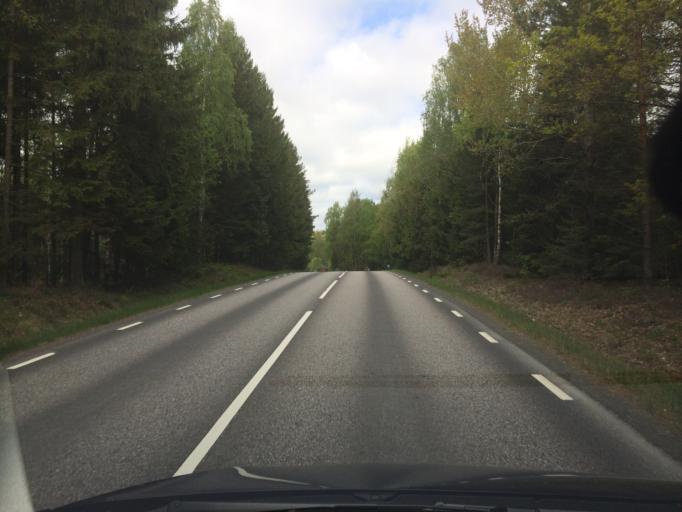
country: SE
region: Vaestra Goetaland
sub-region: Lerums Kommun
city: Stenkullen
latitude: 57.7578
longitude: 12.3171
